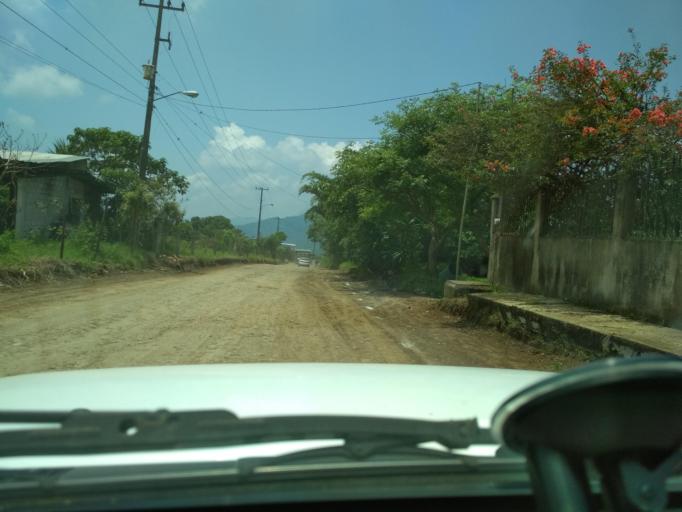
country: MX
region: Veracruz
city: Ixtac Zoquitlan
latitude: 18.8779
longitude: -97.0779
